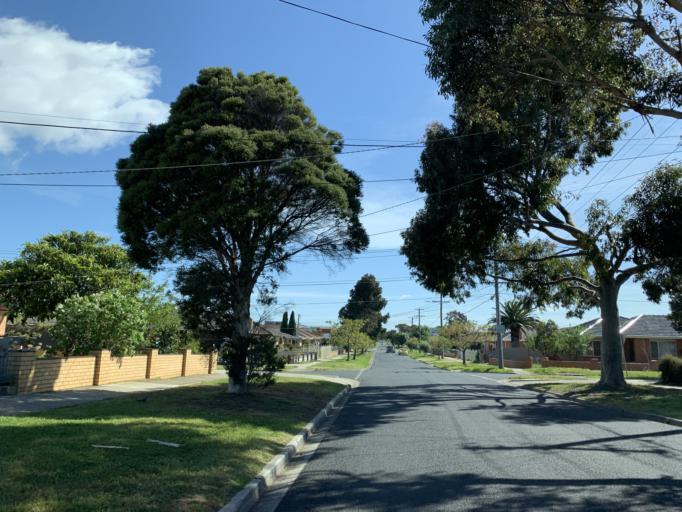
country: AU
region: Victoria
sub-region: Brimbank
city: Saint Albans
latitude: -37.7348
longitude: 144.7994
